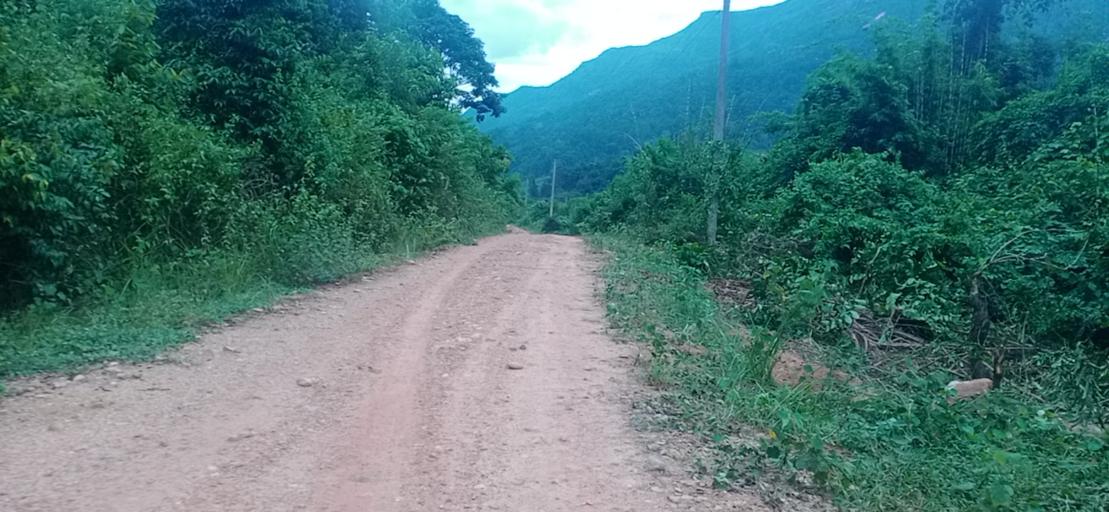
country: TH
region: Changwat Bueng Kan
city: Pak Khat
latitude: 18.5593
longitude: 103.2330
